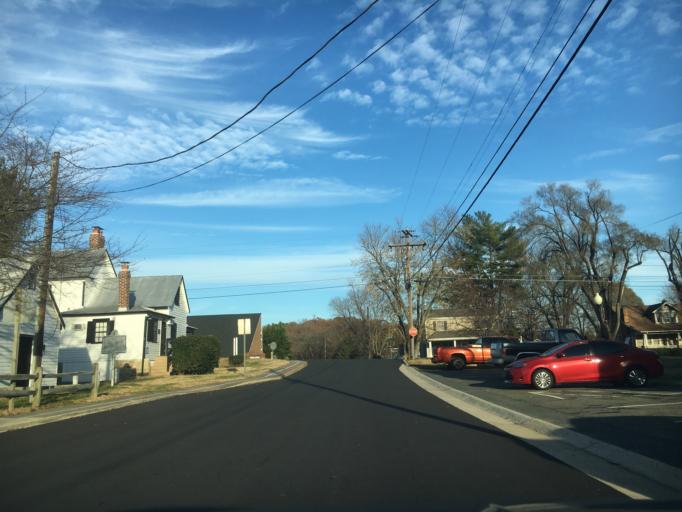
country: US
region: Virginia
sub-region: Prince William County
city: Dumfries
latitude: 38.5683
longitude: -77.3295
